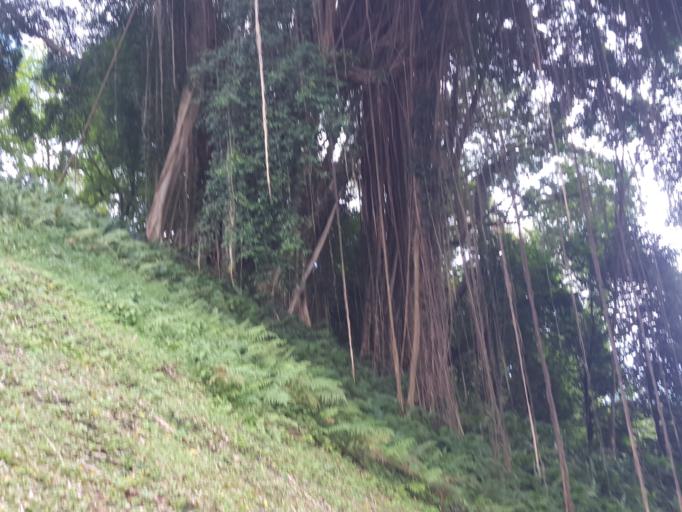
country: SG
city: Singapore
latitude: 1.2940
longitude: 103.8454
